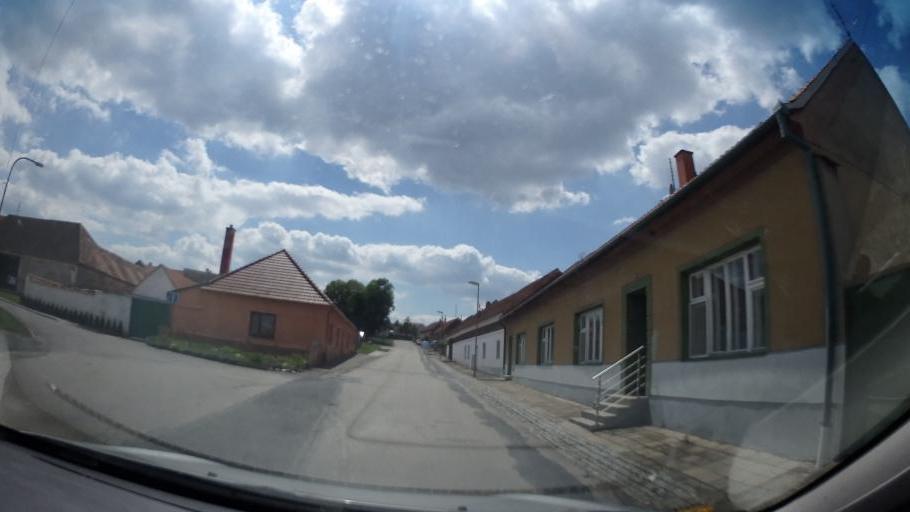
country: CZ
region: Vysocina
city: Mohelno
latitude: 49.1149
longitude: 16.1887
